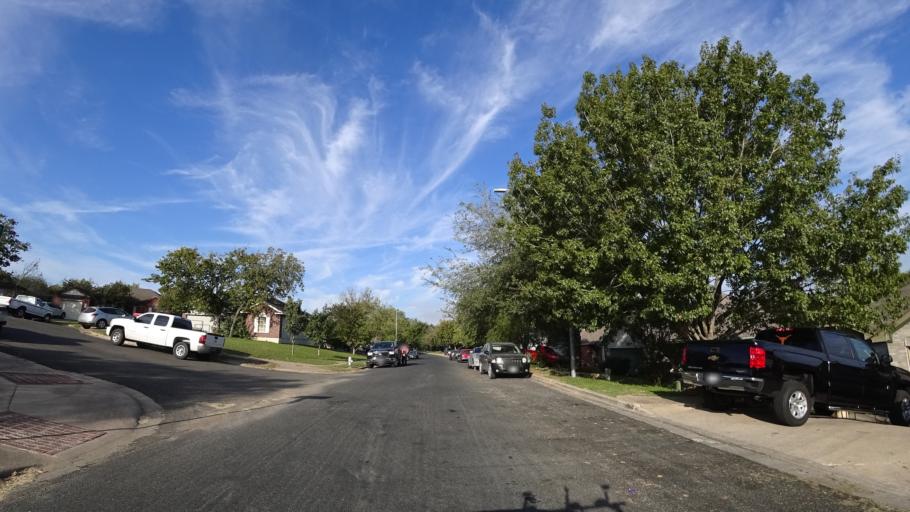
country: US
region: Texas
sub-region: Travis County
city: Austin
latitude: 30.1946
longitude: -97.7347
